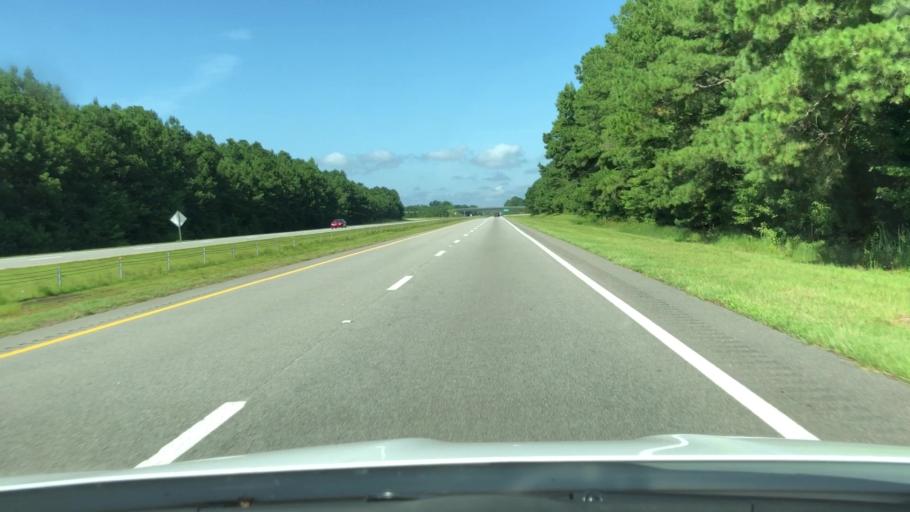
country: US
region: North Carolina
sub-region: Chowan County
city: Edenton
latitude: 36.0624
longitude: -76.6597
